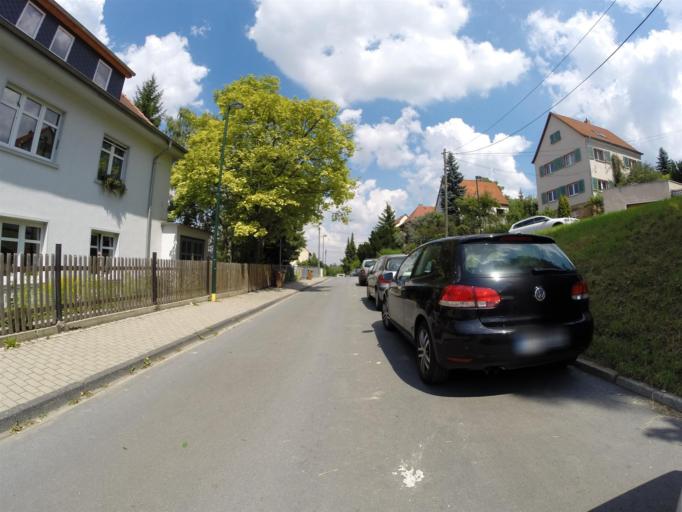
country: DE
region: Thuringia
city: Jena
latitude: 50.9259
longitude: 11.5977
